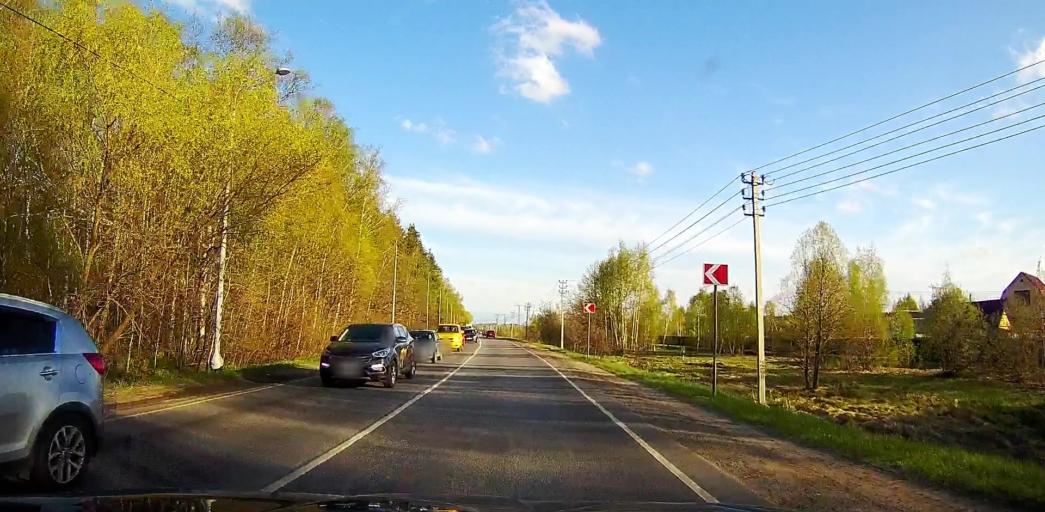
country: RU
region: Moskovskaya
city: Bronnitsy
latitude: 55.3806
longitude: 38.2084
